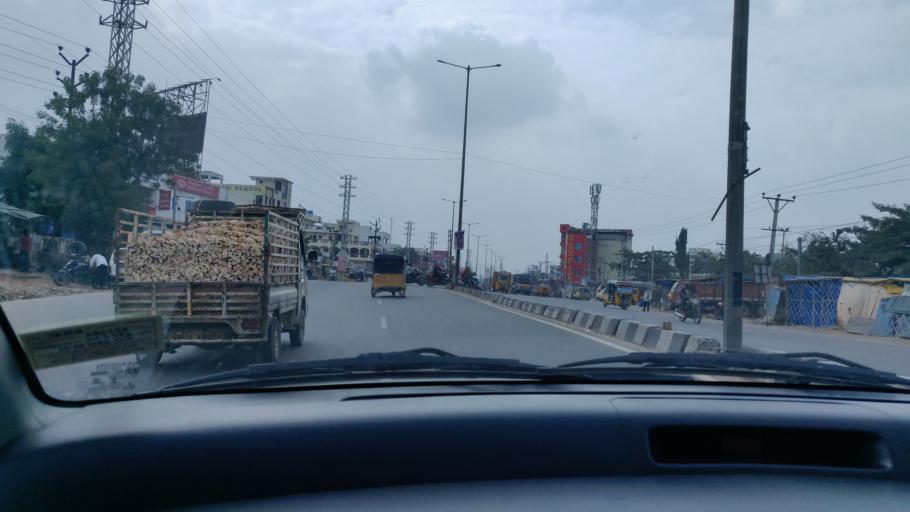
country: IN
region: Telangana
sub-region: Rangareddi
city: Balapur
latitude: 17.3169
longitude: 78.4512
